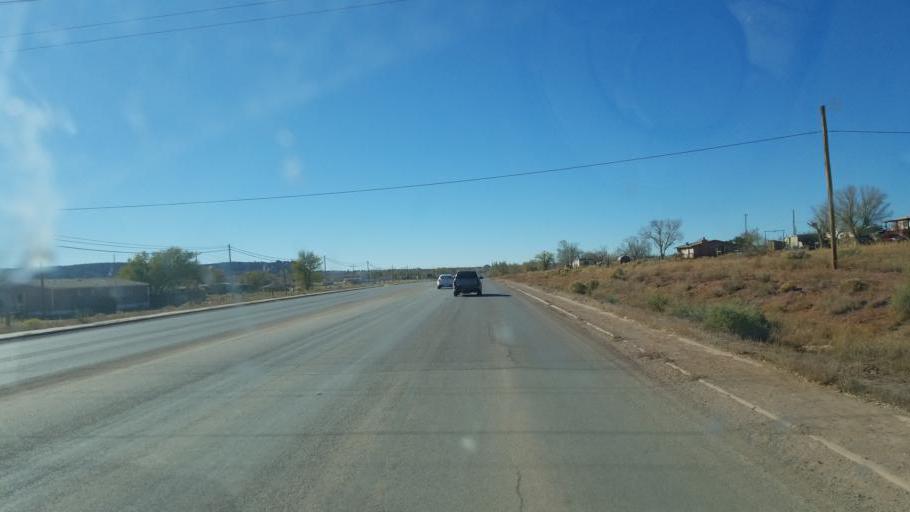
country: US
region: Arizona
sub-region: Apache County
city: Fort Defiance
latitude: 35.7438
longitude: -109.0562
